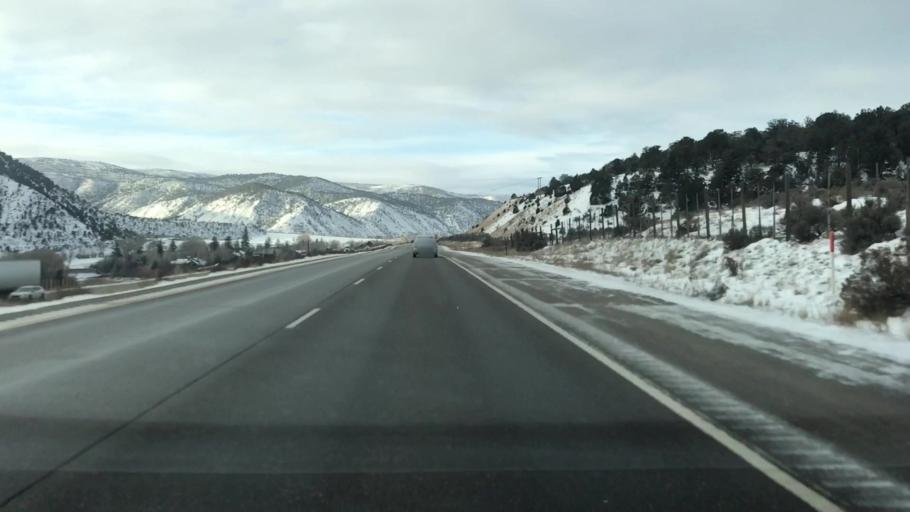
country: US
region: Colorado
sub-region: Eagle County
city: Eagle
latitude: 39.6904
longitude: -106.7496
